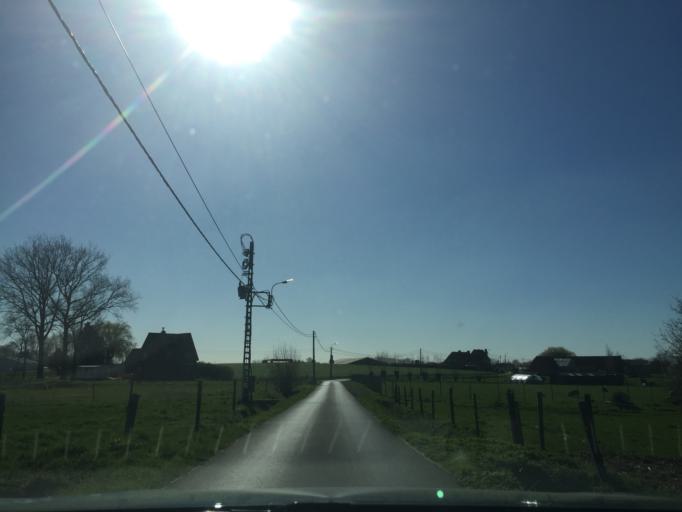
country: BE
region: Flanders
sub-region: Provincie West-Vlaanderen
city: Hooglede
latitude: 50.9752
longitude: 3.0628
